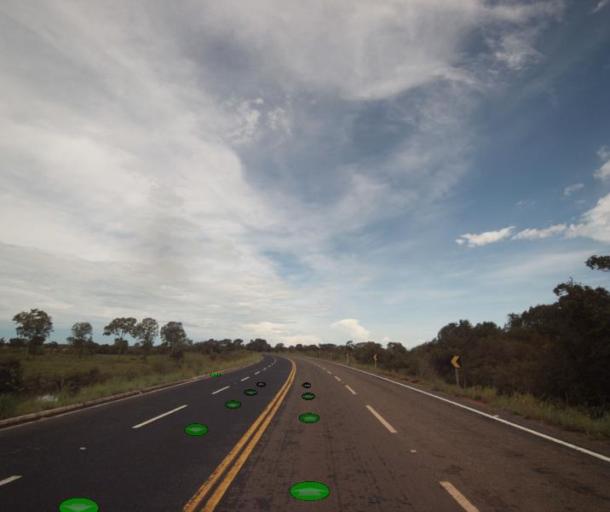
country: BR
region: Goias
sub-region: Sao Miguel Do Araguaia
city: Sao Miguel do Araguaia
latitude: -13.2332
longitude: -50.5638
